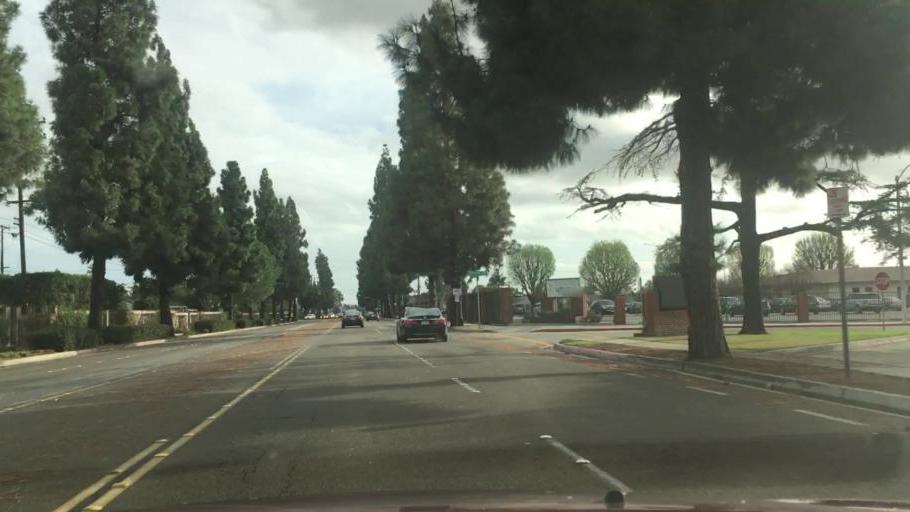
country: US
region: California
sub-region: Los Angeles County
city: East La Mirada
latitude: 33.9383
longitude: -117.9932
